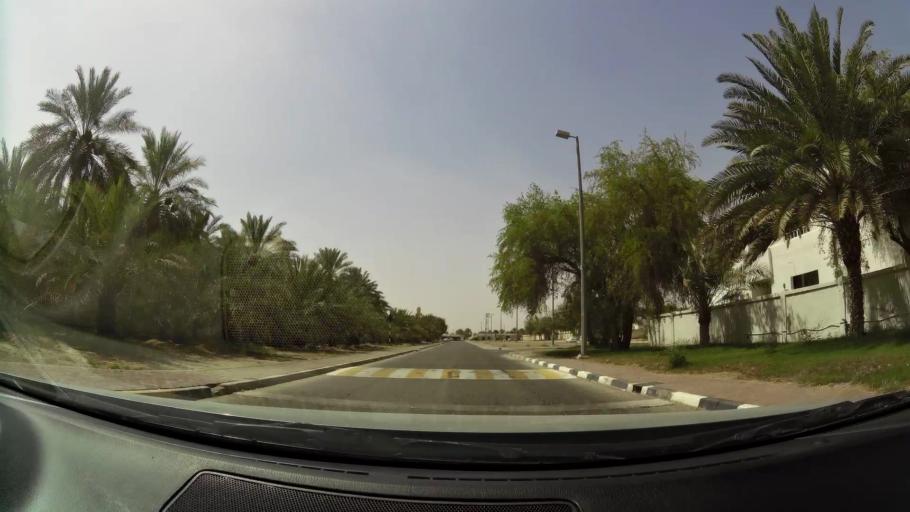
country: AE
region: Abu Dhabi
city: Al Ain
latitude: 24.2254
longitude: 55.7020
